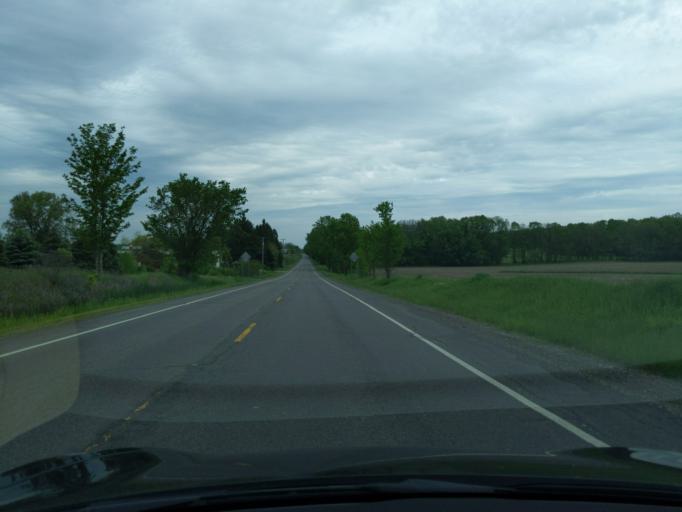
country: US
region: Michigan
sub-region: Ingham County
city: Mason
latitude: 42.5570
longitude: -84.3568
